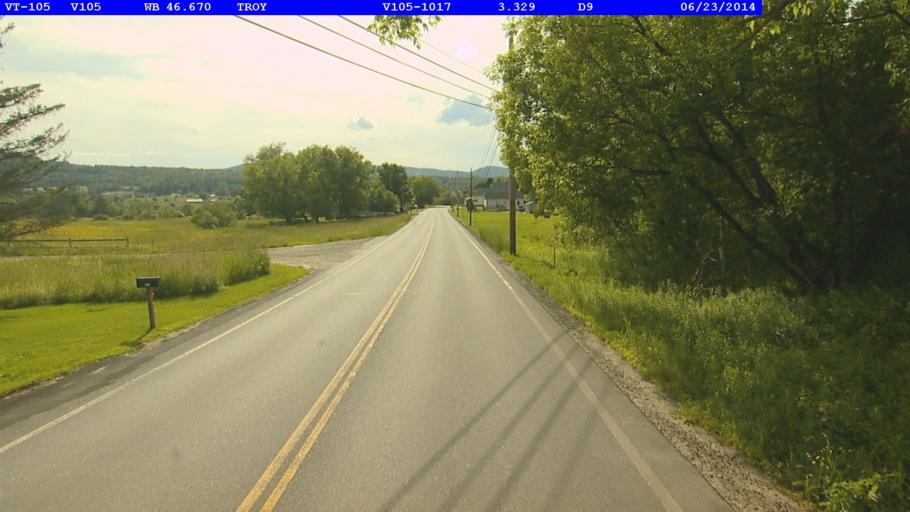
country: US
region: Vermont
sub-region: Orleans County
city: Newport
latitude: 44.9937
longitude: -72.3908
